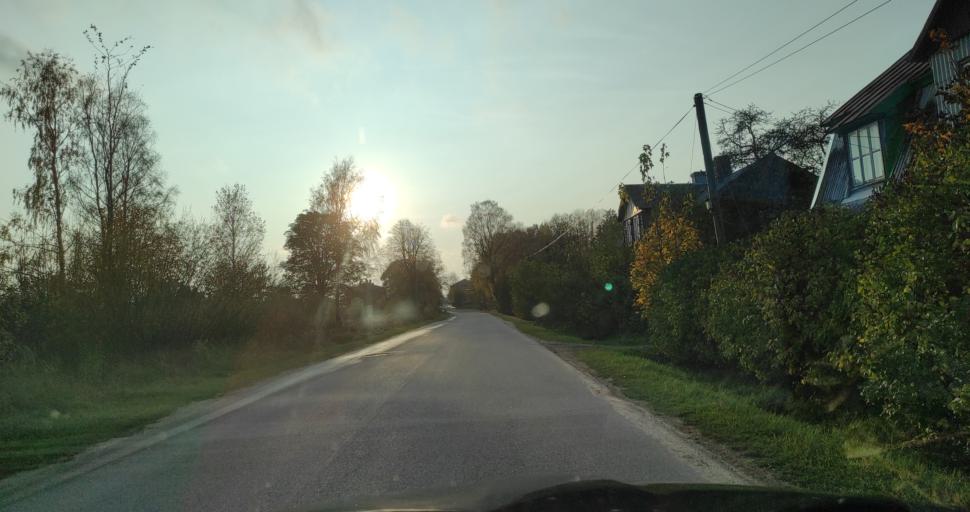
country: LV
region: Vainode
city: Vainode
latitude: 56.4184
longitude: 21.8599
